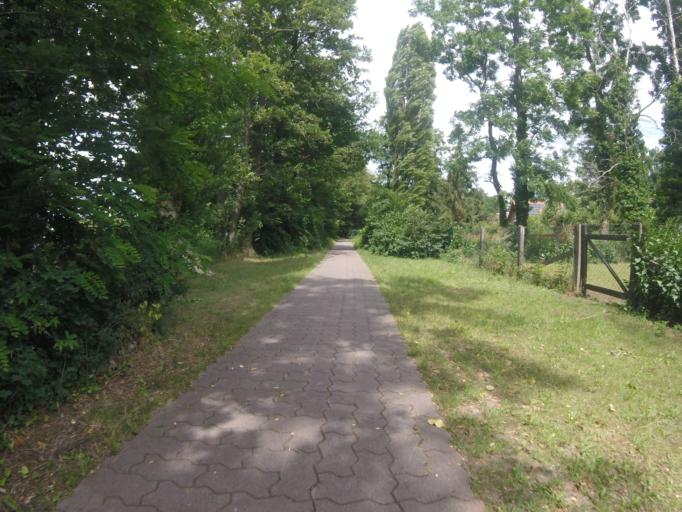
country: DE
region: Brandenburg
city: Bestensee
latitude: 52.2341
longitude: 13.6661
